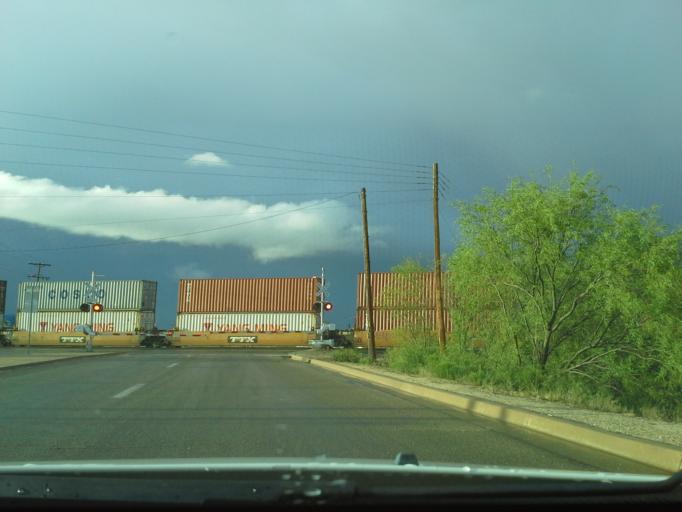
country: US
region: Arizona
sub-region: Cochise County
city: Benson
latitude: 31.9708
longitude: -110.3070
